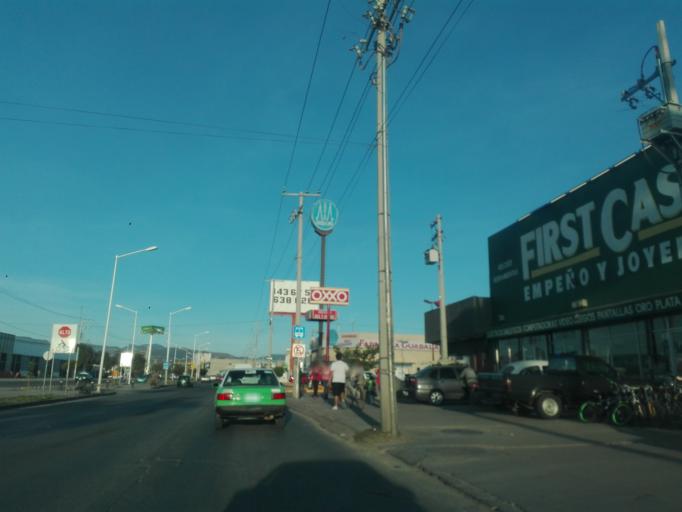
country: MX
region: Guanajuato
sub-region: Leon
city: San Jose de Duran (Los Troncoso)
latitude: 21.0823
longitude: -101.6289
